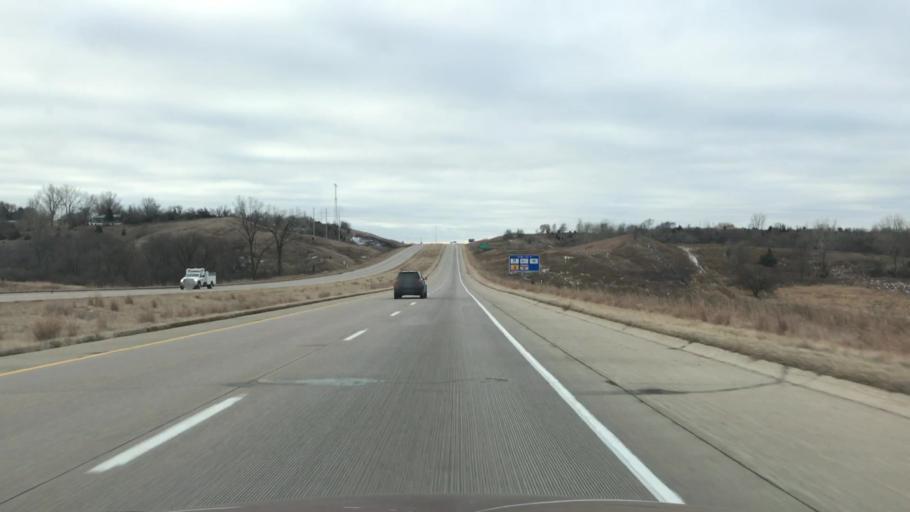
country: US
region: Iowa
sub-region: Woodbury County
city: Sioux City
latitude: 42.4944
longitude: -96.3208
